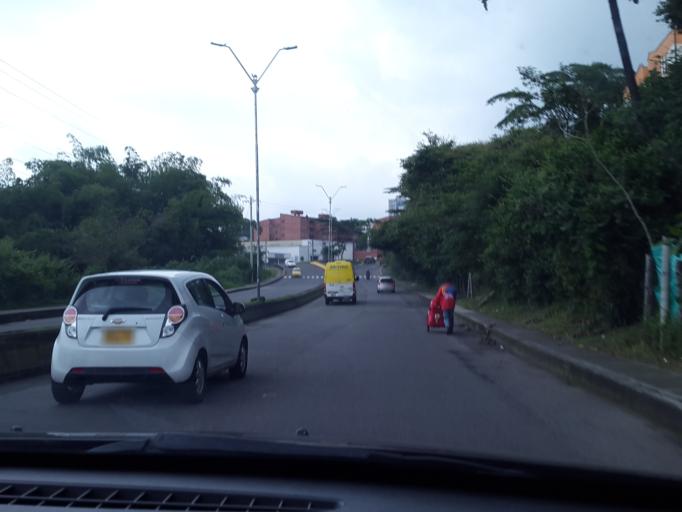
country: CO
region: Quindio
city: Armenia
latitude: 4.5459
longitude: -75.6683
